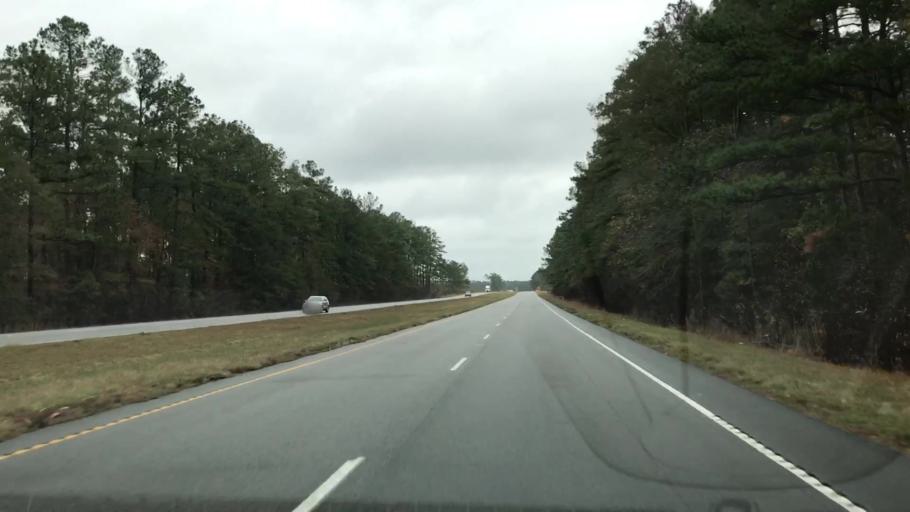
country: US
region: South Carolina
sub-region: Charleston County
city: Awendaw
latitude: 33.1667
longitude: -79.4220
